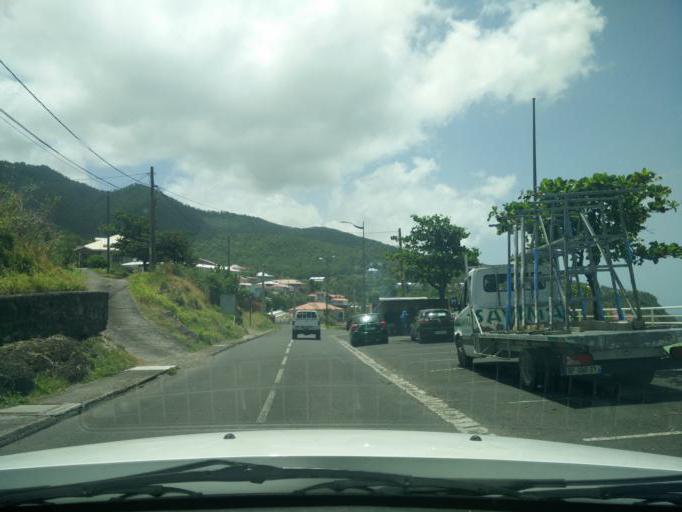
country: GP
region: Guadeloupe
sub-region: Guadeloupe
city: Gourbeyre
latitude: 15.9479
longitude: -61.6969
